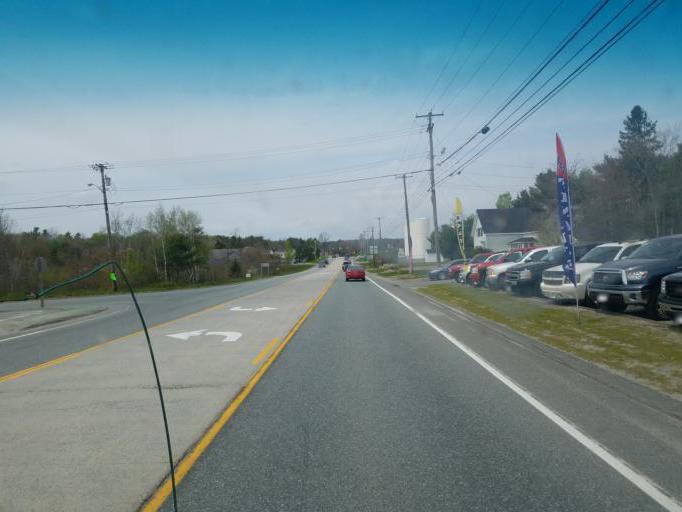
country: US
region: Maine
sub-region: Hancock County
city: Ellsworth
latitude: 44.5677
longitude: -68.4509
